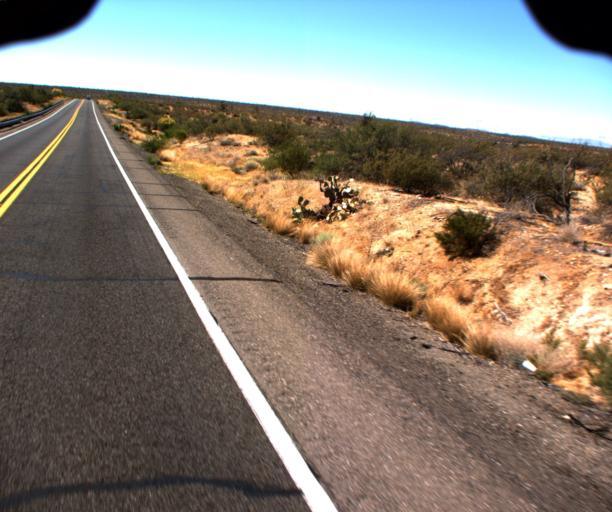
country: US
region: Arizona
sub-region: Yavapai County
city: Congress
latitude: 34.2124
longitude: -113.0662
